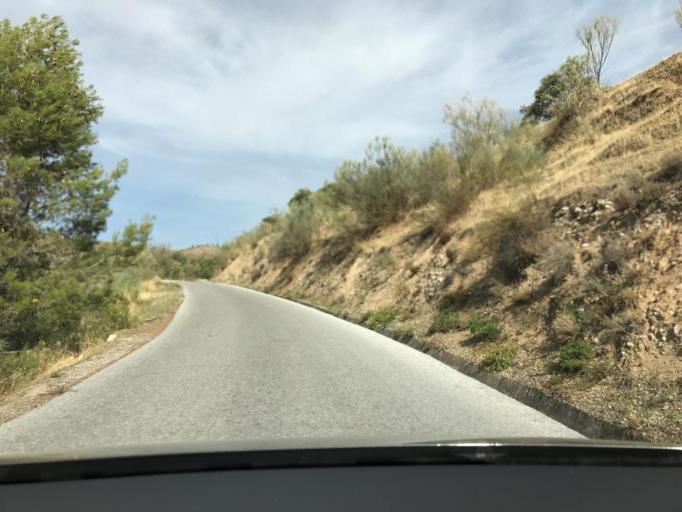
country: ES
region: Andalusia
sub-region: Provincia de Granada
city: Granada
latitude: 37.1848
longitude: -3.5777
